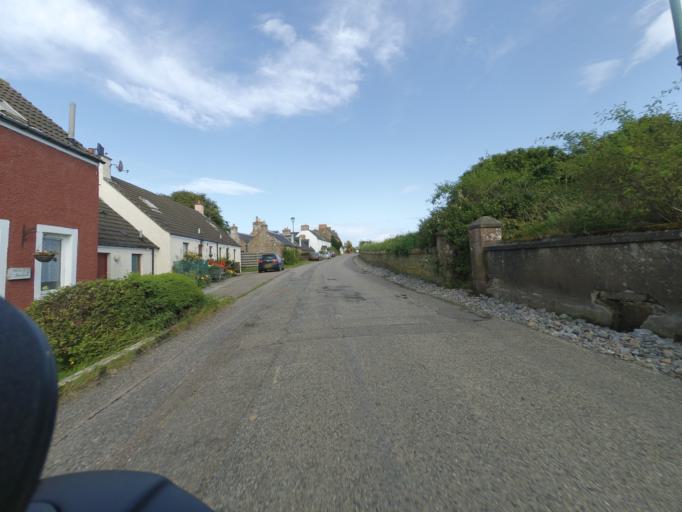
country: GB
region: Scotland
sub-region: Highland
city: Invergordon
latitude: 57.6578
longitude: -4.1520
